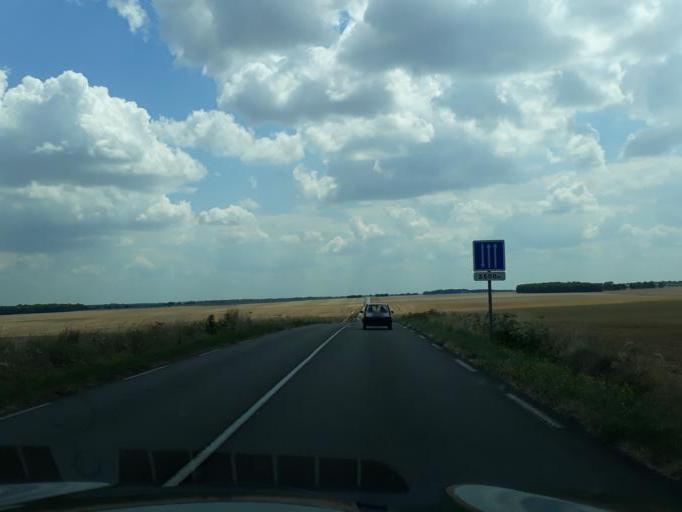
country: FR
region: Centre
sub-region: Departement du Cher
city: Saint-Germain-du-Puy
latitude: 47.0716
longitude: 2.4925
